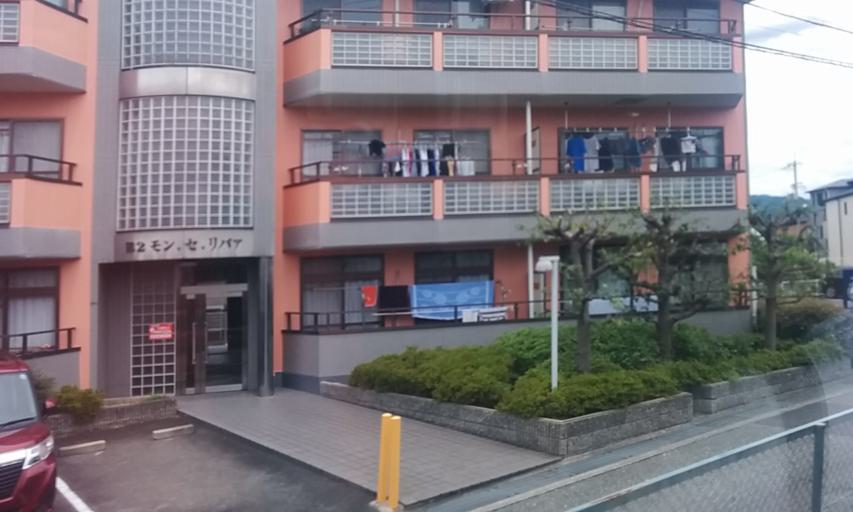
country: JP
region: Osaka
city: Mino
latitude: 34.8138
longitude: 135.4536
